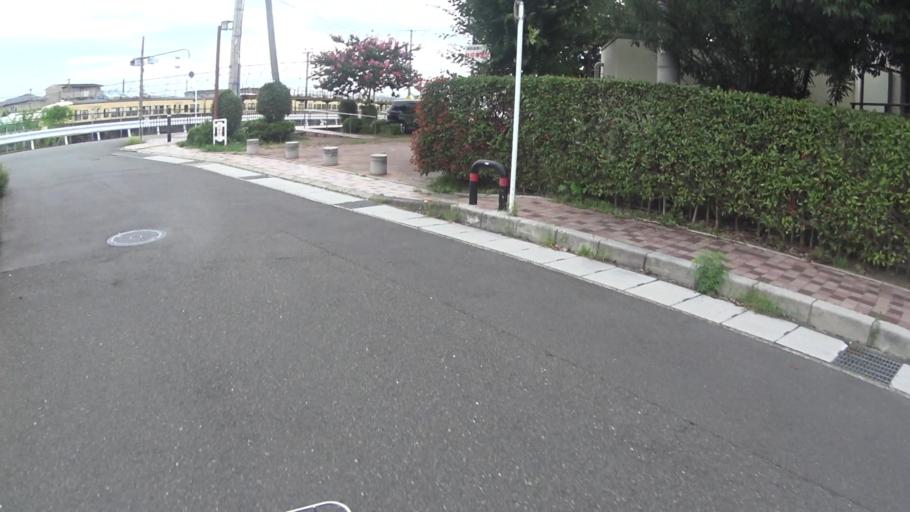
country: JP
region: Kyoto
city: Muko
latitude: 34.9252
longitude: 135.7031
